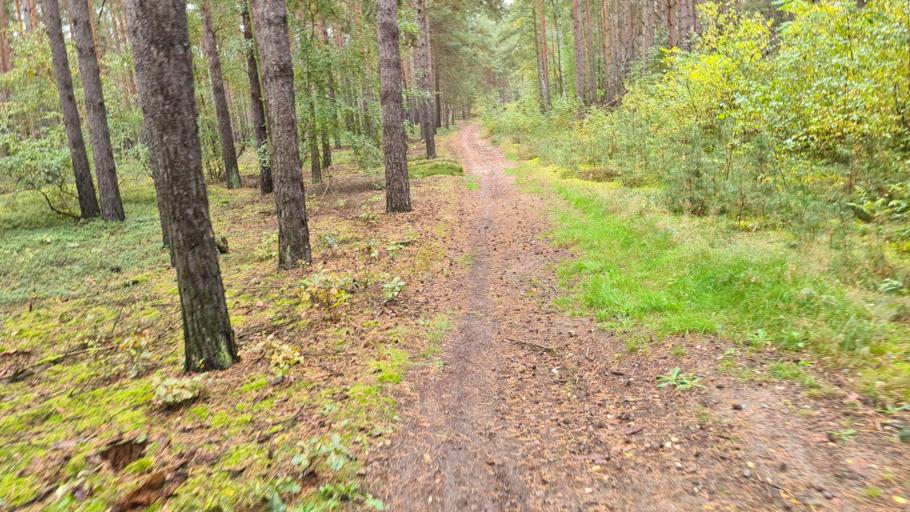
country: DE
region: Brandenburg
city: Schonewalde
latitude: 51.6300
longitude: 13.6189
